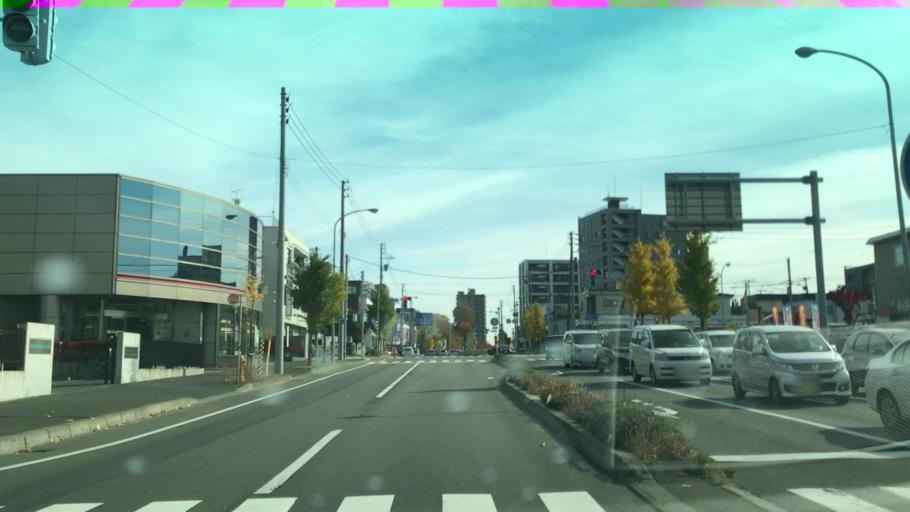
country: JP
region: Hokkaido
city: Sapporo
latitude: 43.0911
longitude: 141.2755
